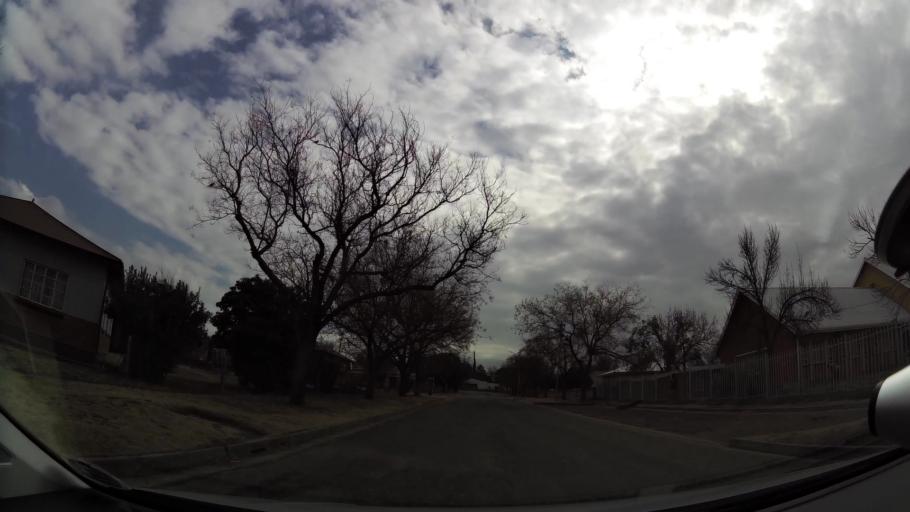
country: ZA
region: Orange Free State
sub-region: Fezile Dabi District Municipality
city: Kroonstad
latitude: -27.6532
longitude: 27.2389
